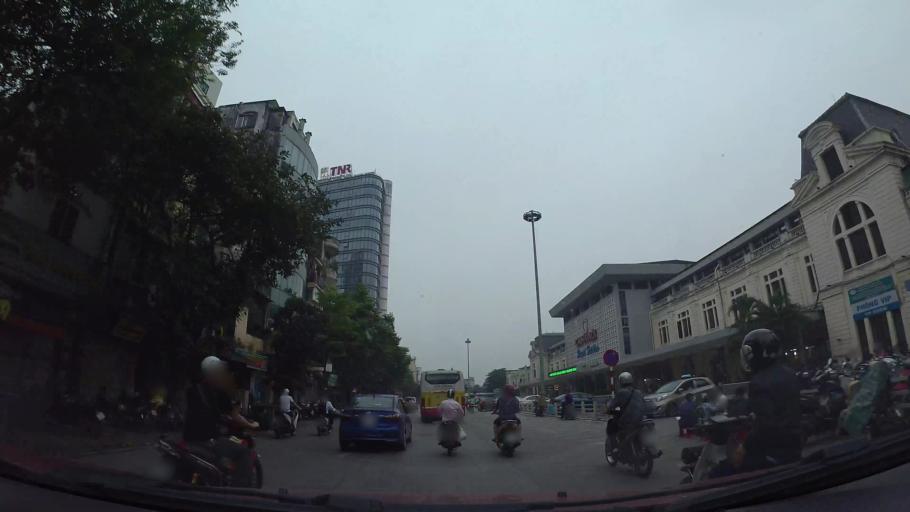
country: VN
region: Ha Noi
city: Hanoi
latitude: 21.0249
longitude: 105.8414
